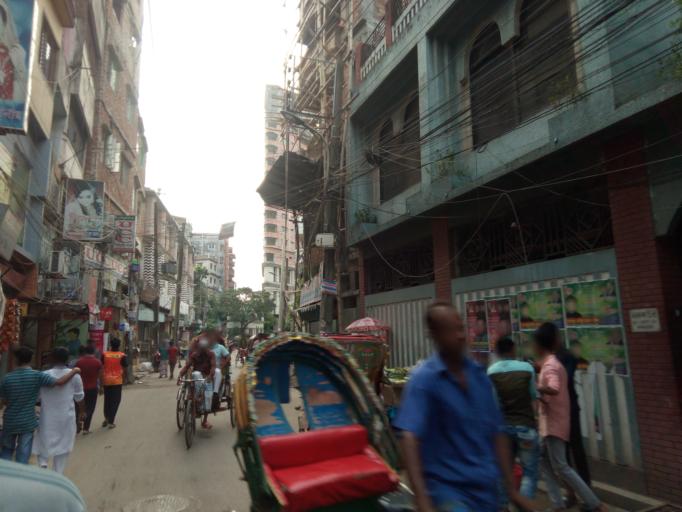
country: BD
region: Dhaka
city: Azimpur
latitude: 23.7210
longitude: 90.3887
